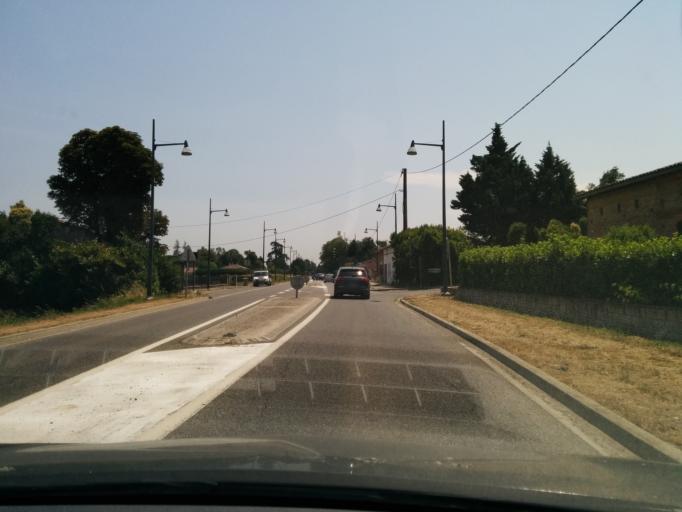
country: FR
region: Midi-Pyrenees
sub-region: Departement de la Haute-Garonne
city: Pompertuzat
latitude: 43.4975
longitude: 1.5177
